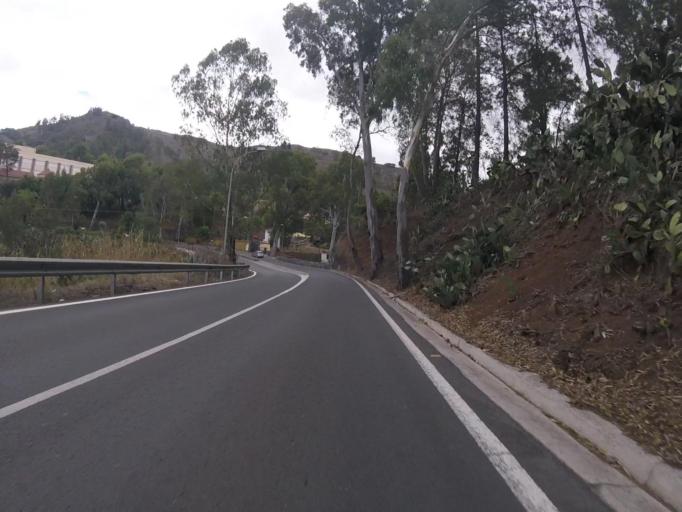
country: ES
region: Canary Islands
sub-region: Provincia de Las Palmas
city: Santa Brigida
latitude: 28.0274
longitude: -15.5012
